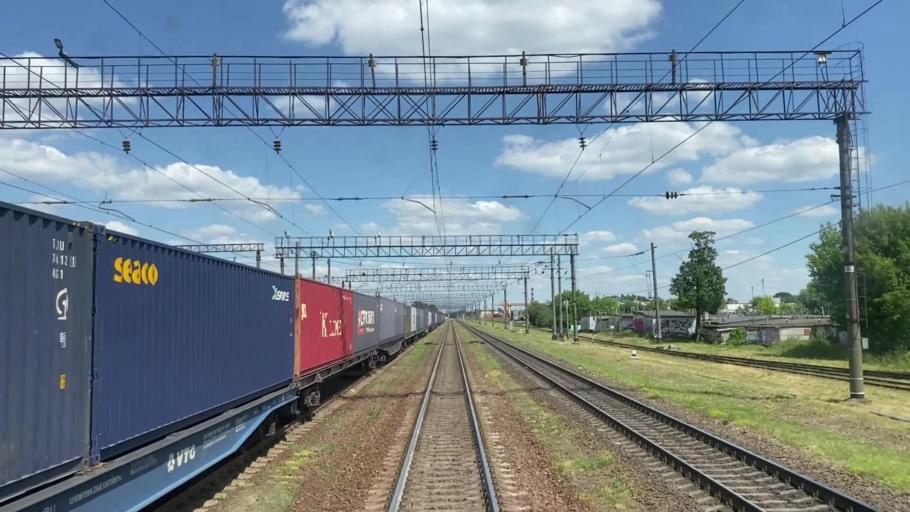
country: BY
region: Brest
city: Brest
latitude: 52.1149
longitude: 23.7540
